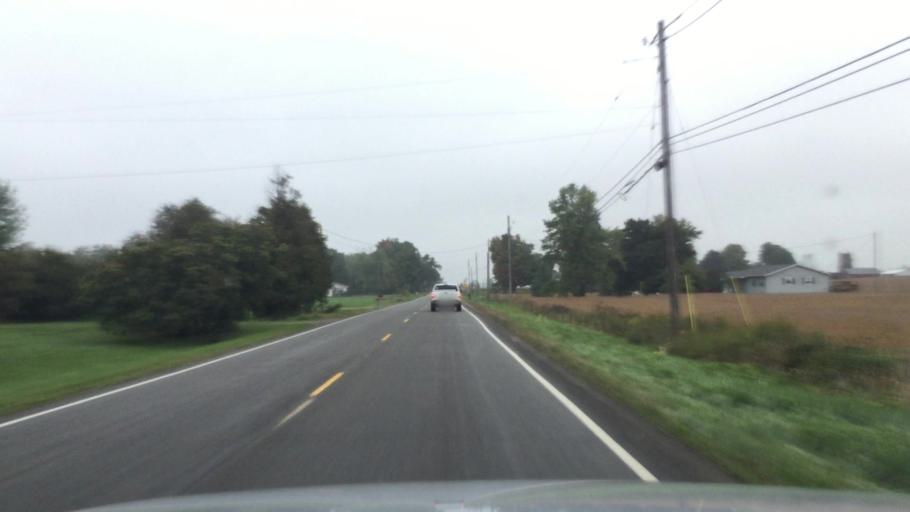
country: US
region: Michigan
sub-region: Shiawassee County
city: Corunna
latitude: 42.9057
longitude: -84.1237
